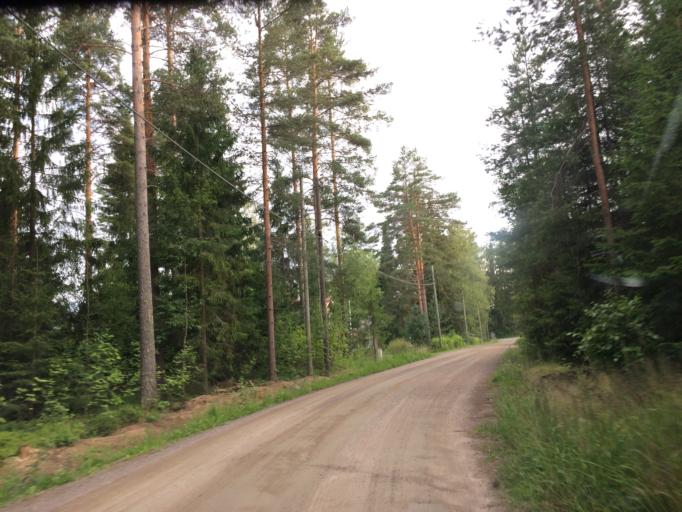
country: FI
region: Haeme
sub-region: Haemeenlinna
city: Tervakoski
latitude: 60.8514
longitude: 24.6236
